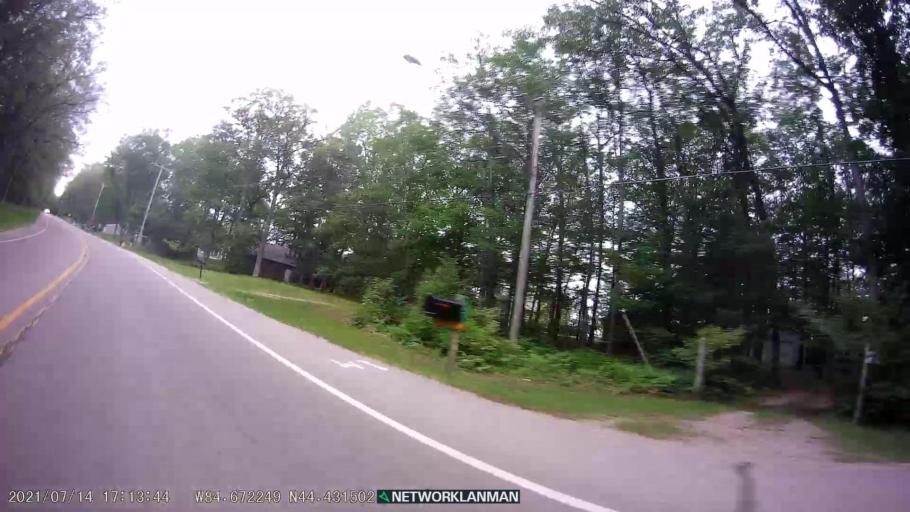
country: US
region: Michigan
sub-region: Roscommon County
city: Roscommon
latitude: 44.4312
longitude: -84.6724
